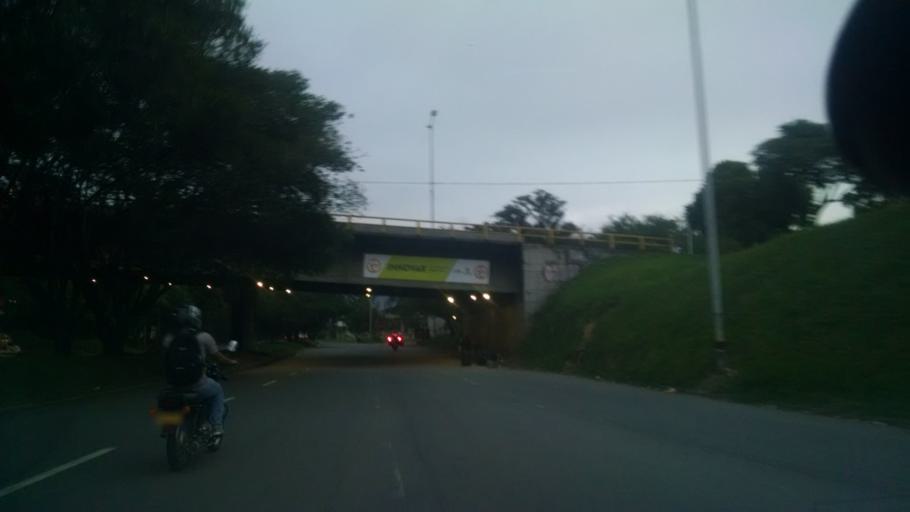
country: CO
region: Antioquia
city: Medellin
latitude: 6.2752
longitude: -75.5692
